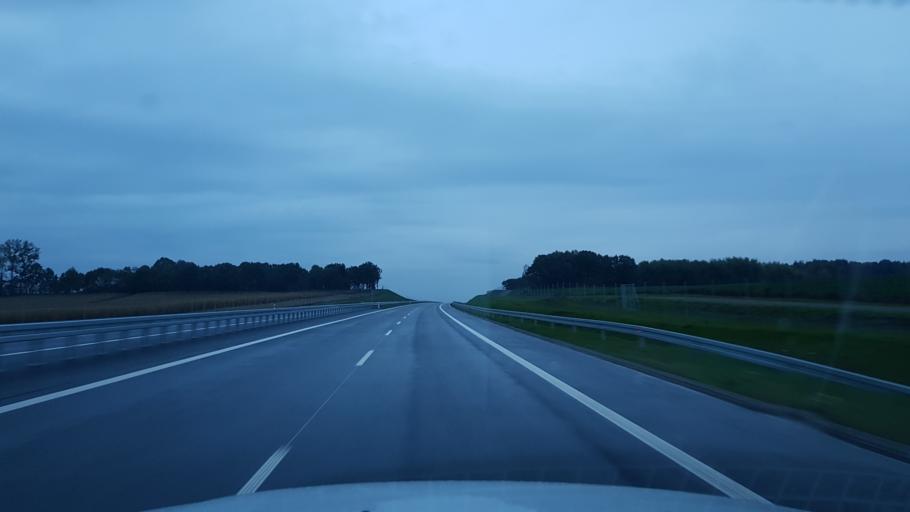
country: PL
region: West Pomeranian Voivodeship
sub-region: Powiat gryficki
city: Brojce
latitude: 53.9092
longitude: 15.3812
